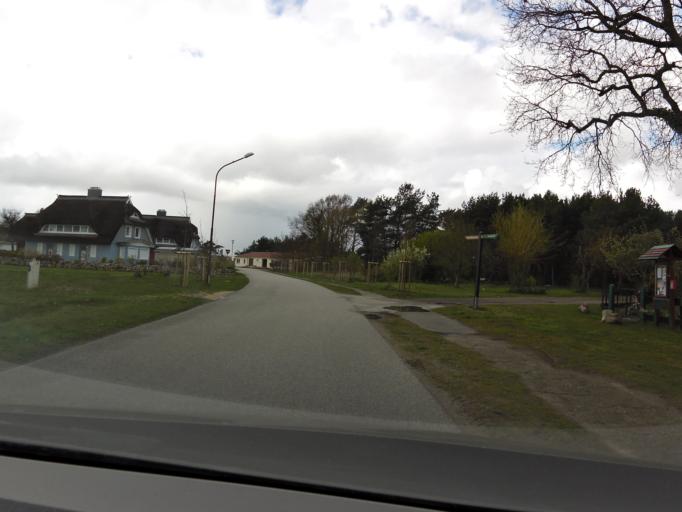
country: DE
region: Mecklenburg-Vorpommern
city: Born
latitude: 54.3831
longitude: 12.5128
